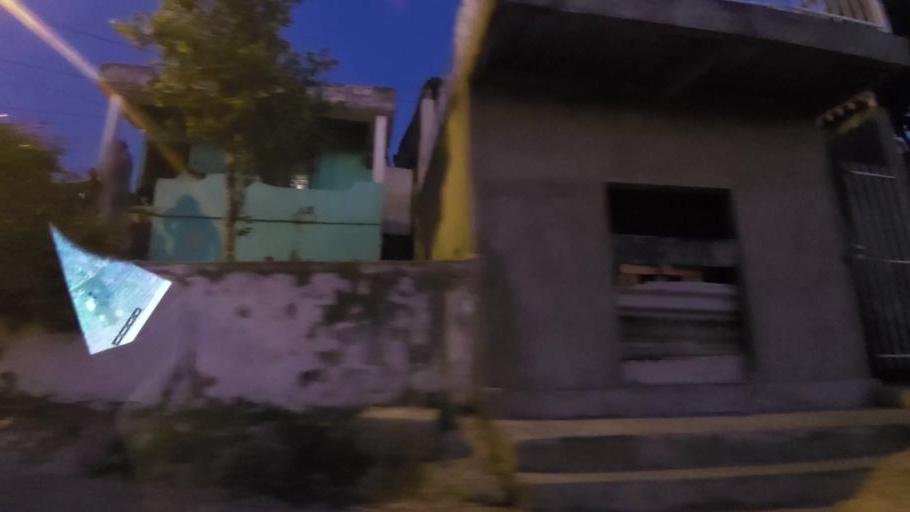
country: CO
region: Bolivar
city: Cartagena
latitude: 10.4011
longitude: -75.5093
